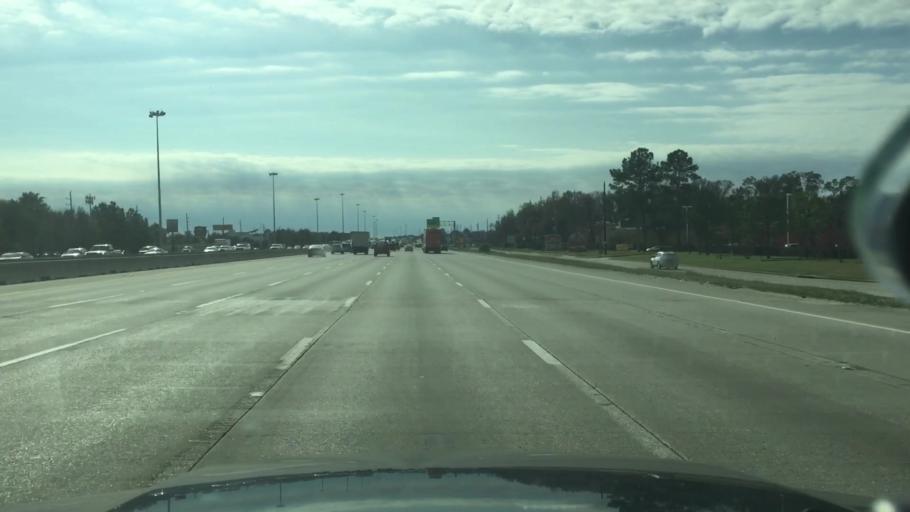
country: US
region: Texas
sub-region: Harris County
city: Aldine
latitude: 29.9893
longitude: -95.4242
